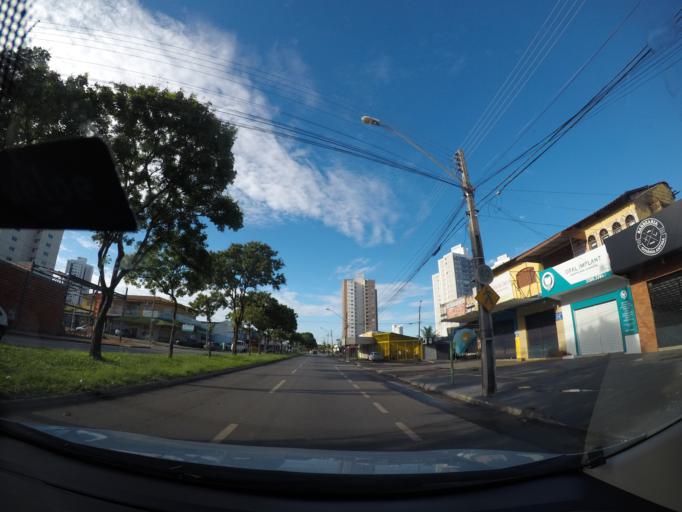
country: BR
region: Goias
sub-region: Goiania
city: Goiania
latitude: -16.7338
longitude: -49.2725
